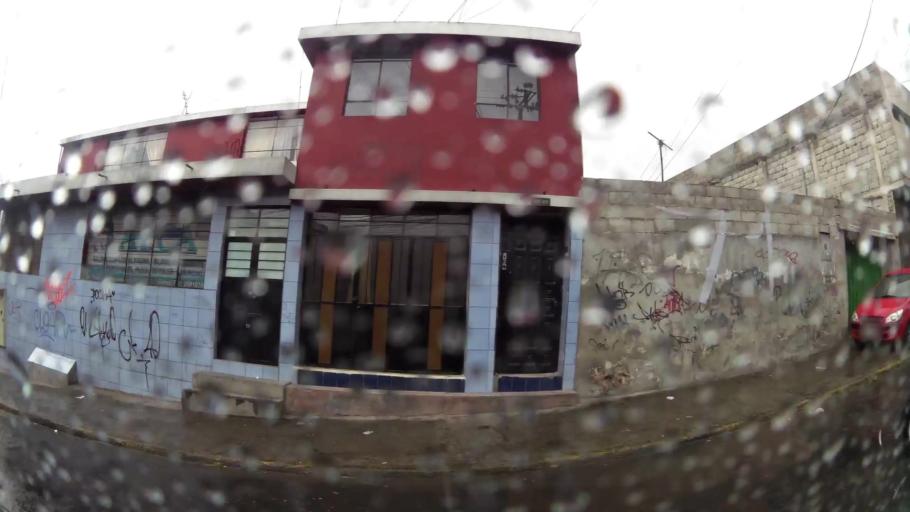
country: EC
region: Pichincha
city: Quito
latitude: -0.1079
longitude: -78.4969
